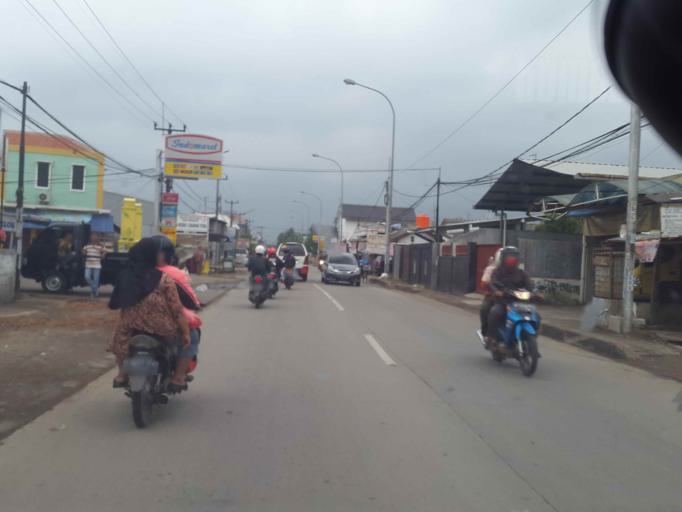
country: ID
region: West Java
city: Cikarang
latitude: -6.2751
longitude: 107.1724
